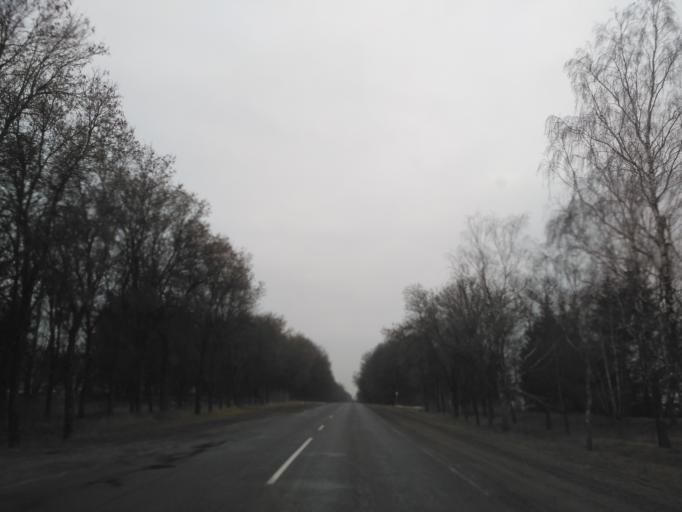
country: BY
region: Minsk
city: Snow
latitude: 53.2405
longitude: 26.2453
